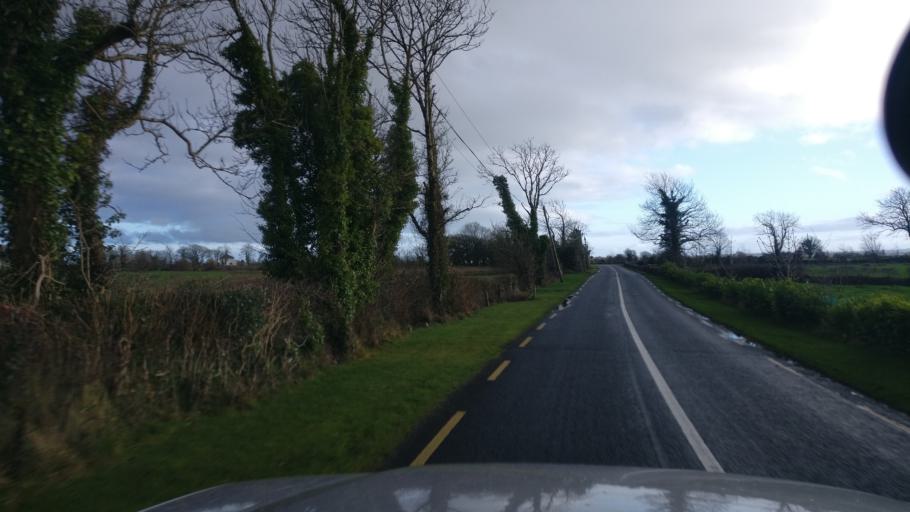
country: IE
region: Connaught
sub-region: County Galway
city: Athenry
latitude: 53.2942
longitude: -8.6483
